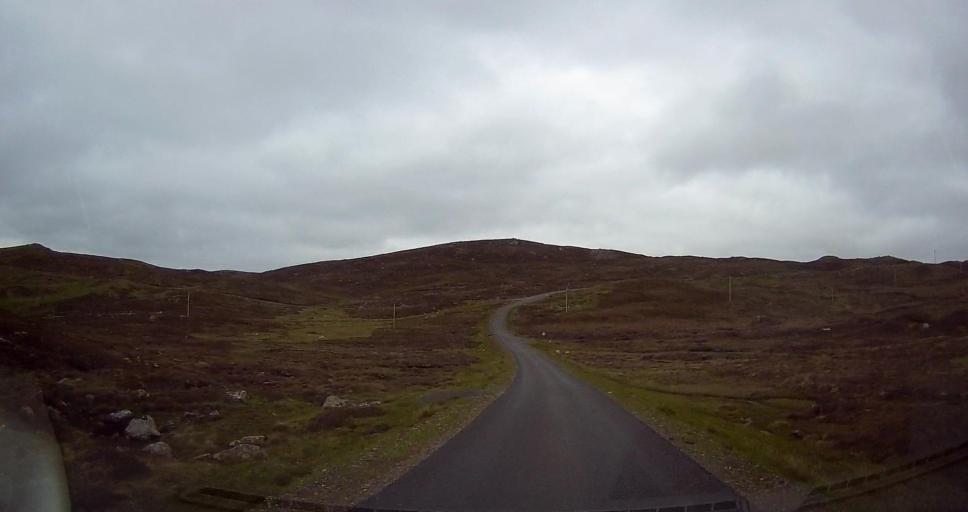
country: GB
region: Scotland
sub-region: Shetland Islands
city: Lerwick
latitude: 60.3381
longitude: -1.3191
